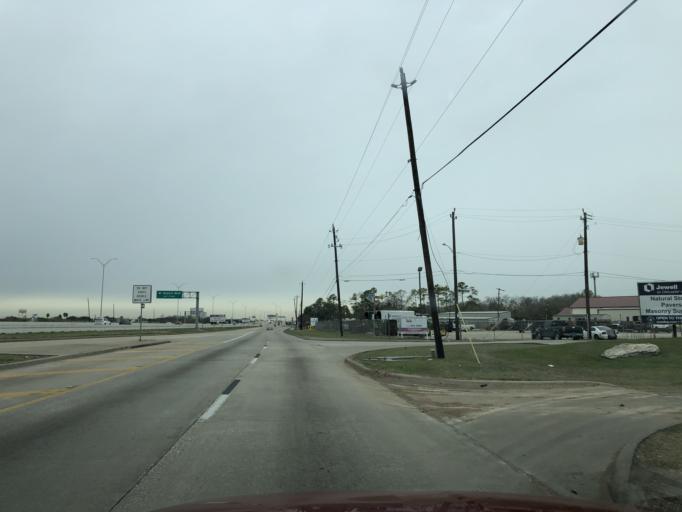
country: US
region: Texas
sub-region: Fort Bend County
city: Missouri City
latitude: 29.6308
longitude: -95.5225
